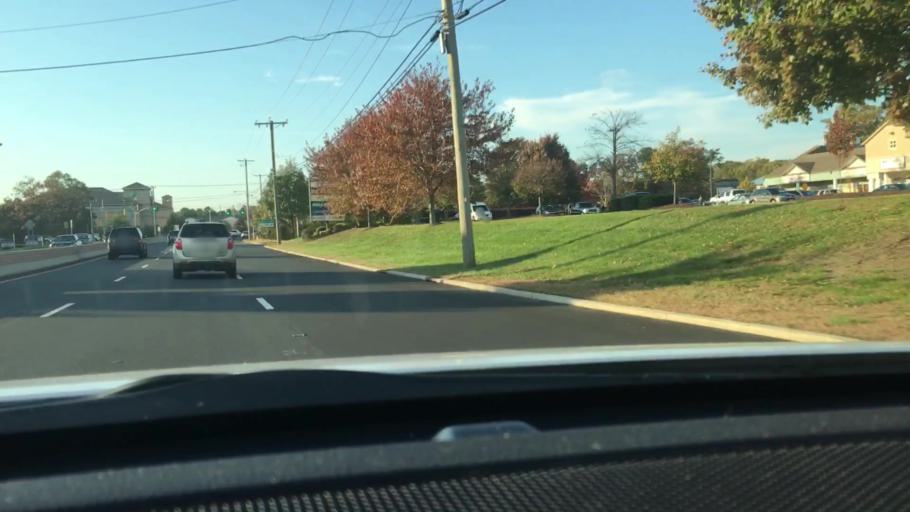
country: US
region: New Jersey
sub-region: Atlantic County
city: Absecon
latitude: 39.4347
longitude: -74.5149
